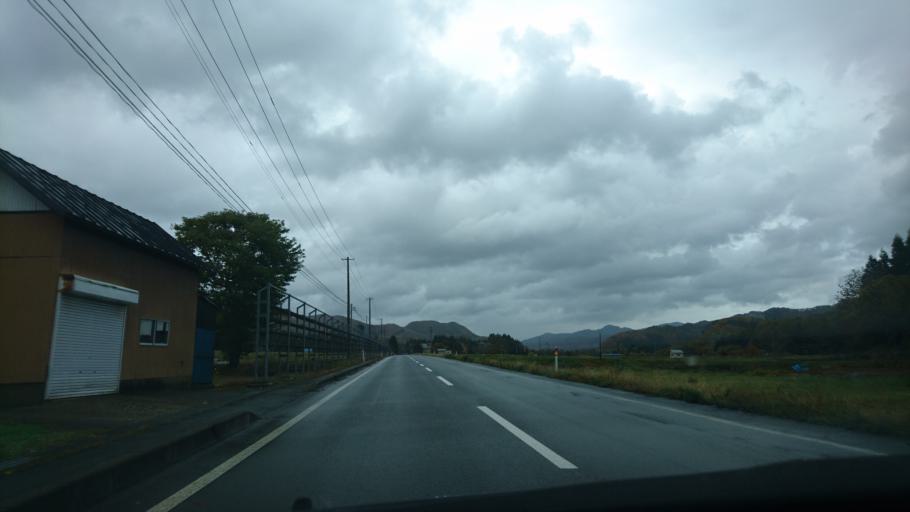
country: JP
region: Akita
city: Kakunodatemachi
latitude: 39.4629
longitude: 140.7766
